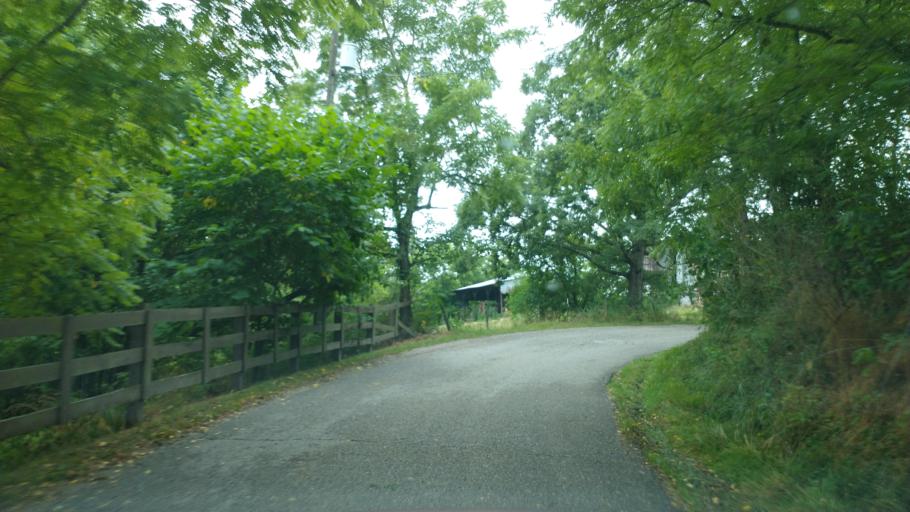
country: US
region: West Virginia
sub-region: Mason County
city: New Haven
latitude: 38.9246
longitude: -81.9673
